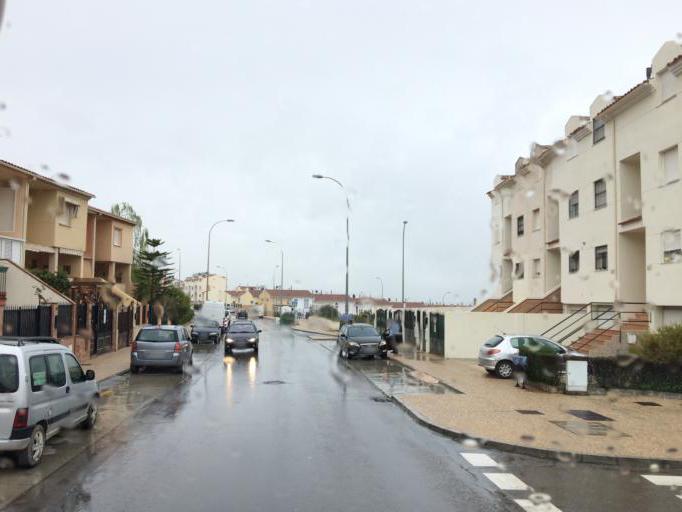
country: ES
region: Andalusia
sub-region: Provincia de Malaga
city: Antequera
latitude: 37.0255
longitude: -4.5534
